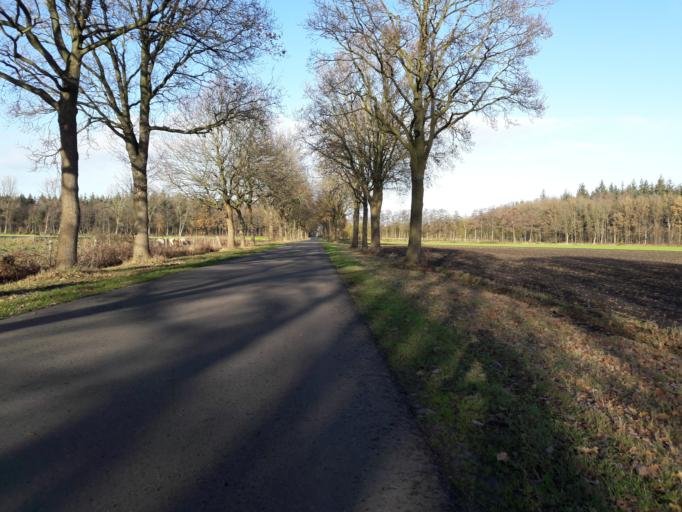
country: NL
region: Drenthe
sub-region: Gemeente Borger-Odoorn
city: Borger
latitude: 52.9203
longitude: 6.7098
